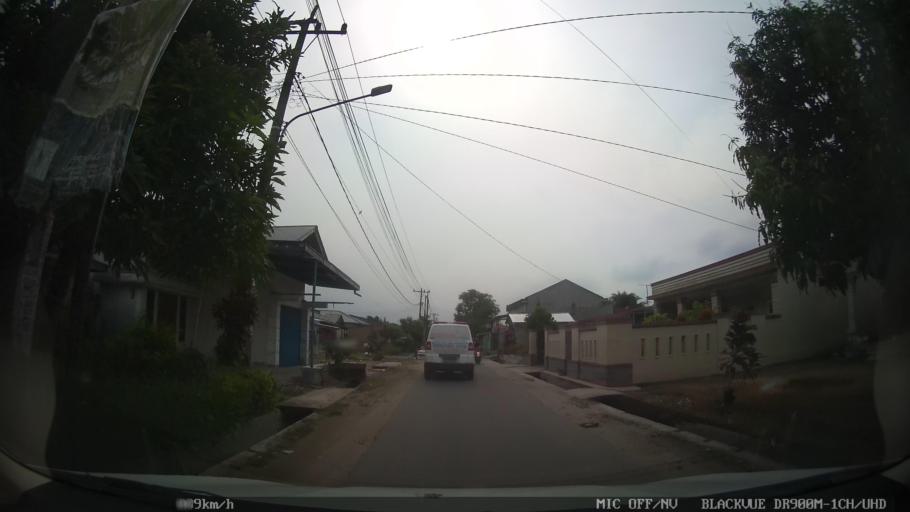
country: ID
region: North Sumatra
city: Medan
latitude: 3.5695
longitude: 98.7555
